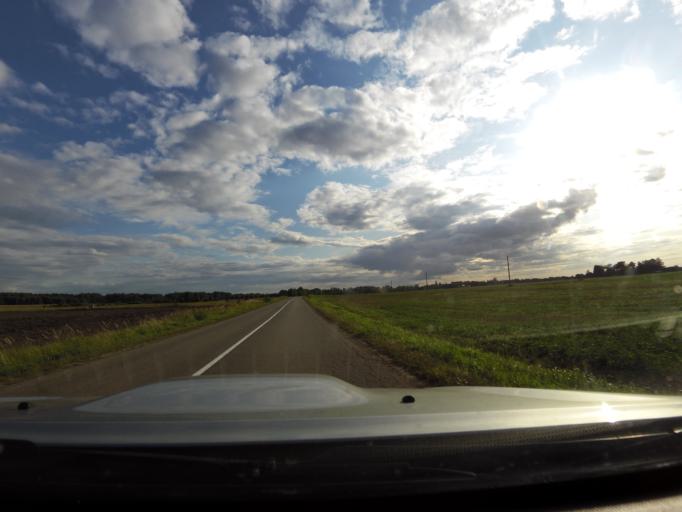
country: LV
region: Nereta
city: Nereta
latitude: 56.0709
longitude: 25.3066
